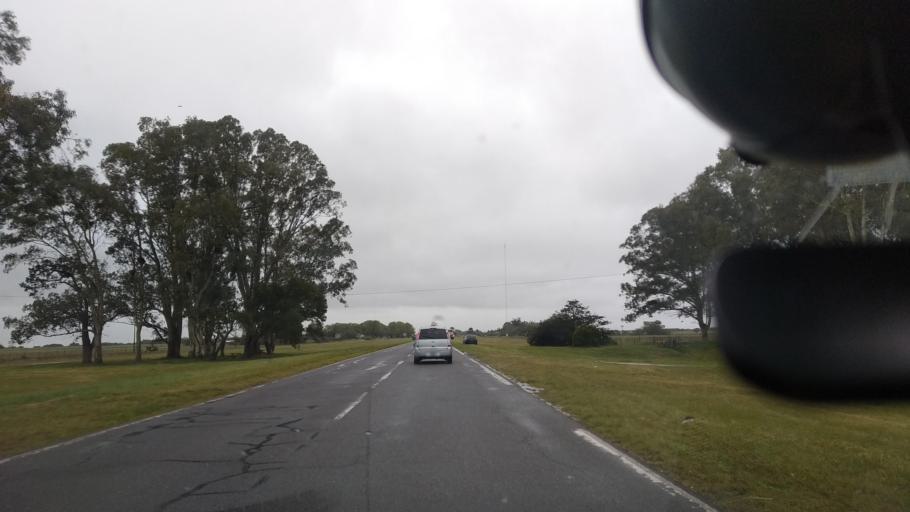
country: AR
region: Buenos Aires
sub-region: Partido de Castelli
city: Castelli
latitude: -35.9836
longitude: -57.4497
